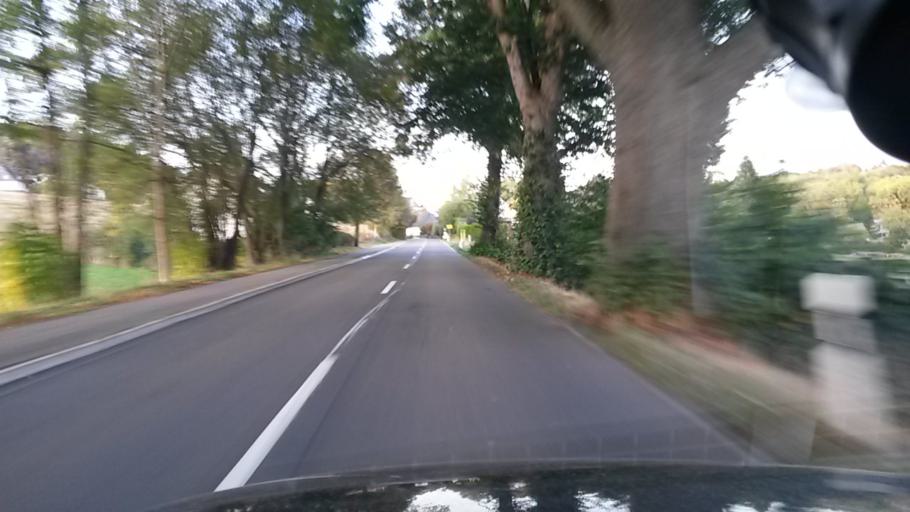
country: DE
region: North Rhine-Westphalia
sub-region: Regierungsbezirk Koln
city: Marienheide
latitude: 51.0731
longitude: 7.5191
